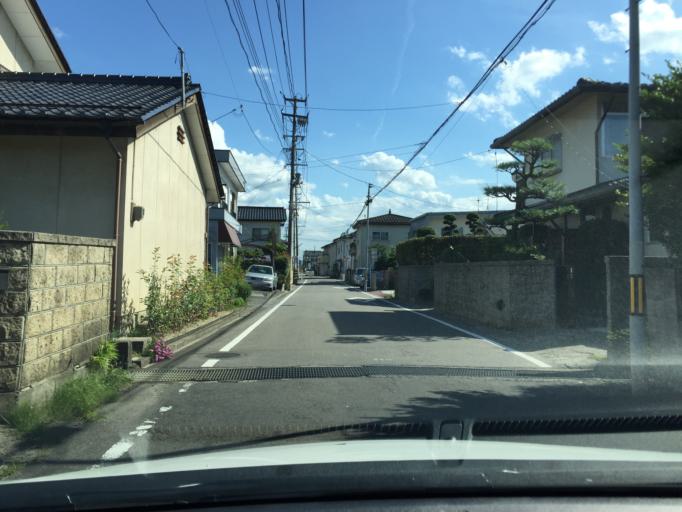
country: JP
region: Fukushima
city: Fukushima-shi
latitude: 37.7728
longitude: 140.4446
